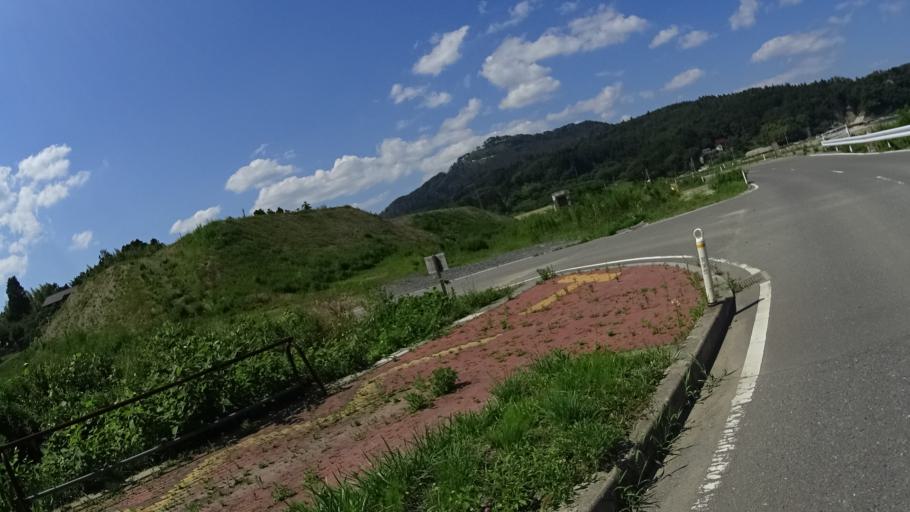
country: JP
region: Iwate
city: Ofunato
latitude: 38.8599
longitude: 141.6215
